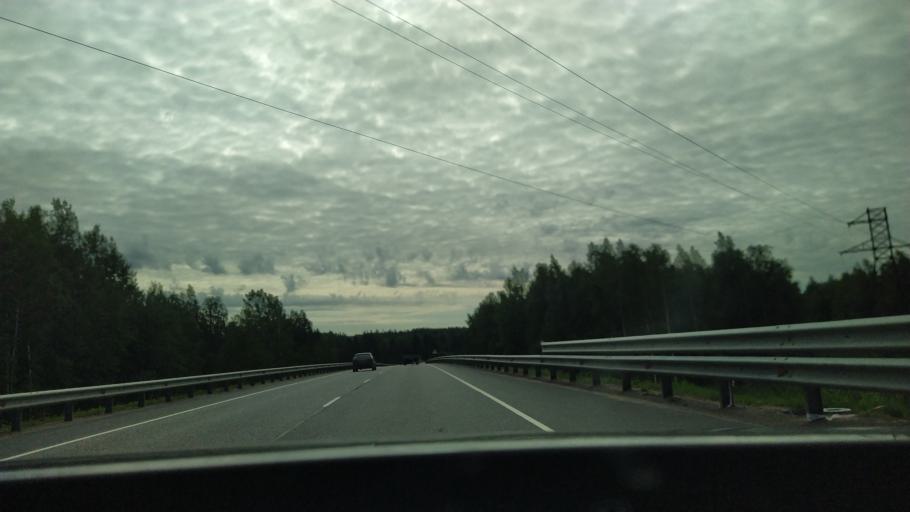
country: RU
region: Leningrad
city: Ul'yanovka
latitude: 59.5930
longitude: 30.7794
